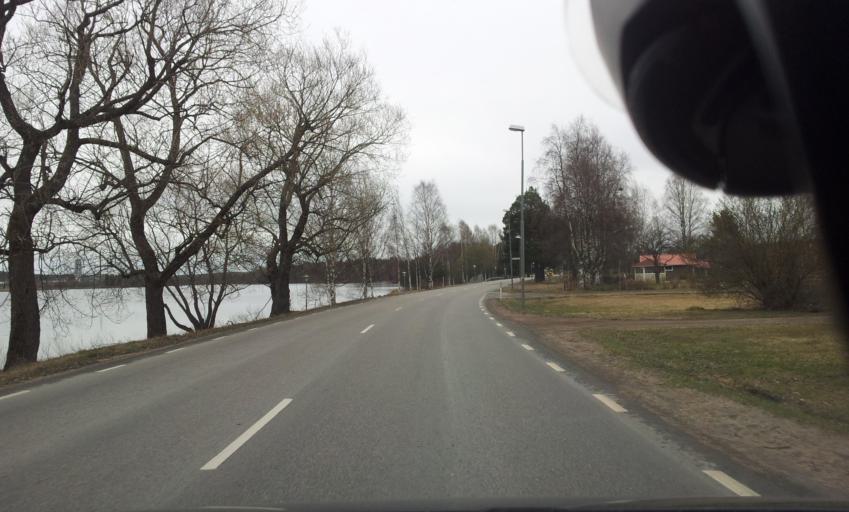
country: SE
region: Gaevleborg
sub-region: Ljusdals Kommun
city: Ljusdal
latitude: 61.8245
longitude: 16.0730
